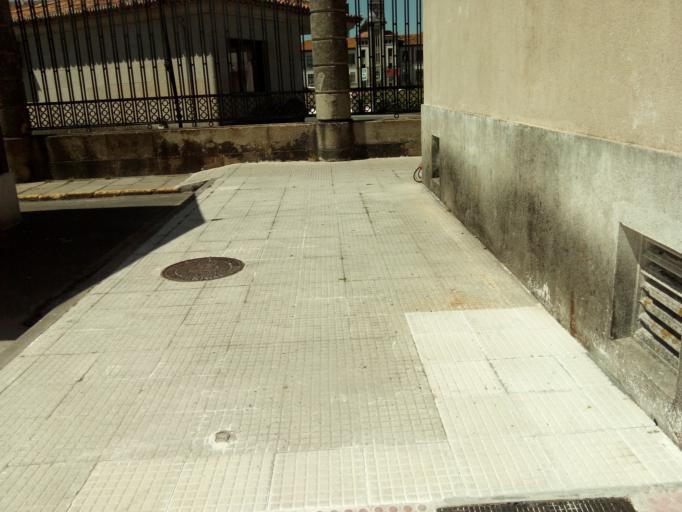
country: ES
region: Galicia
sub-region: Provincia de Pontevedra
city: Marin
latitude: 42.3938
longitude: -8.7026
